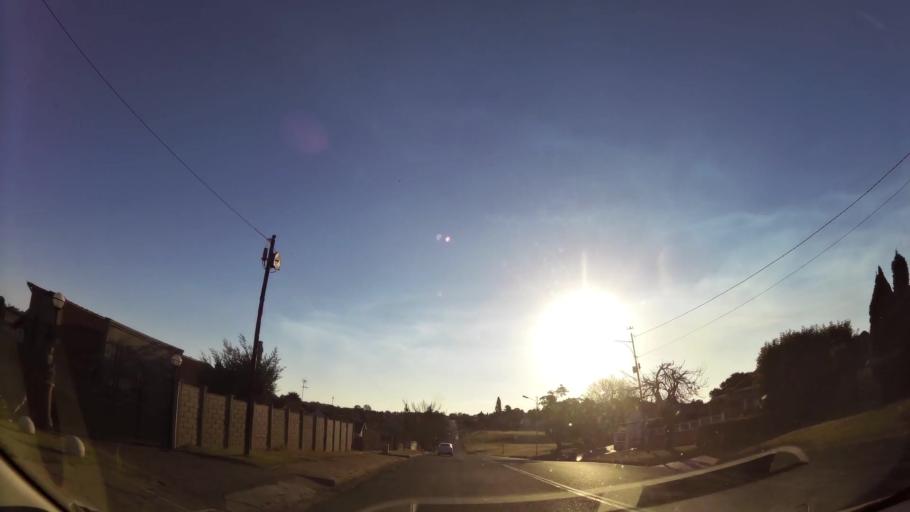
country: ZA
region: Gauteng
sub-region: City of Johannesburg Metropolitan Municipality
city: Roodepoort
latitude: -26.1647
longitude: 27.8866
